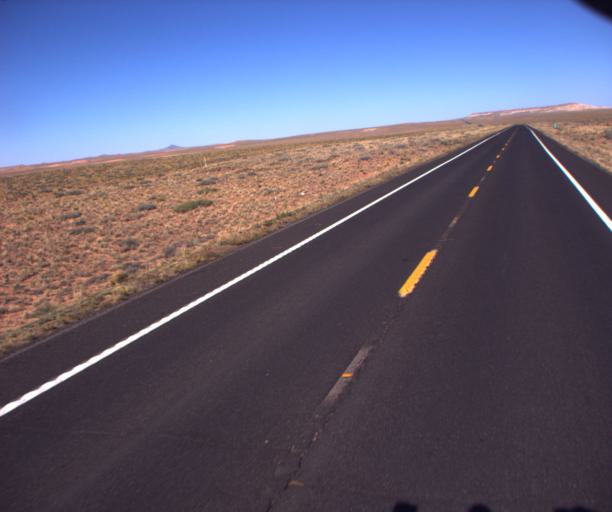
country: US
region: Arizona
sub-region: Coconino County
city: Tuba City
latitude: 36.1750
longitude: -111.0824
